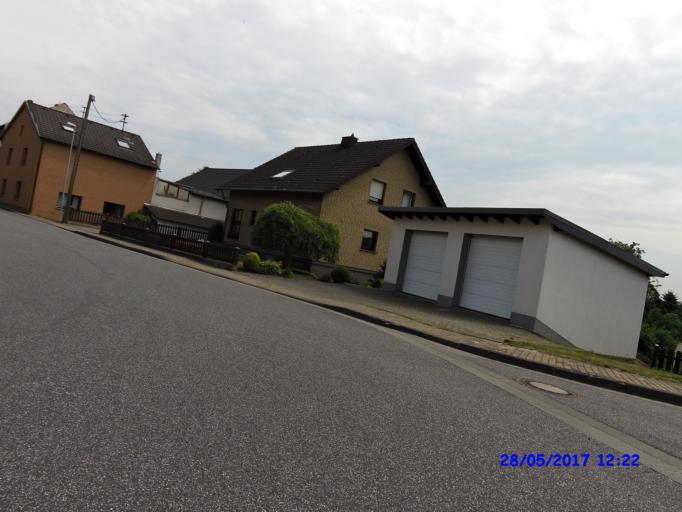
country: DE
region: Rheinland-Pfalz
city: Berg
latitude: 50.5531
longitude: 6.9459
